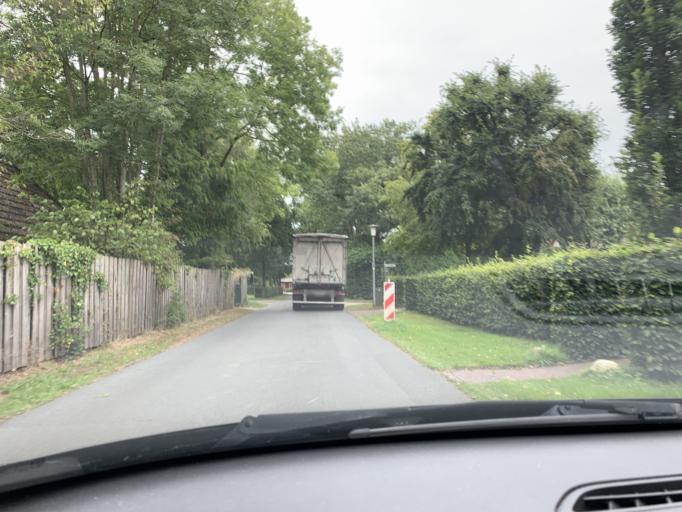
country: DE
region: Lower Saxony
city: Westerstede
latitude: 53.2735
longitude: 7.8991
